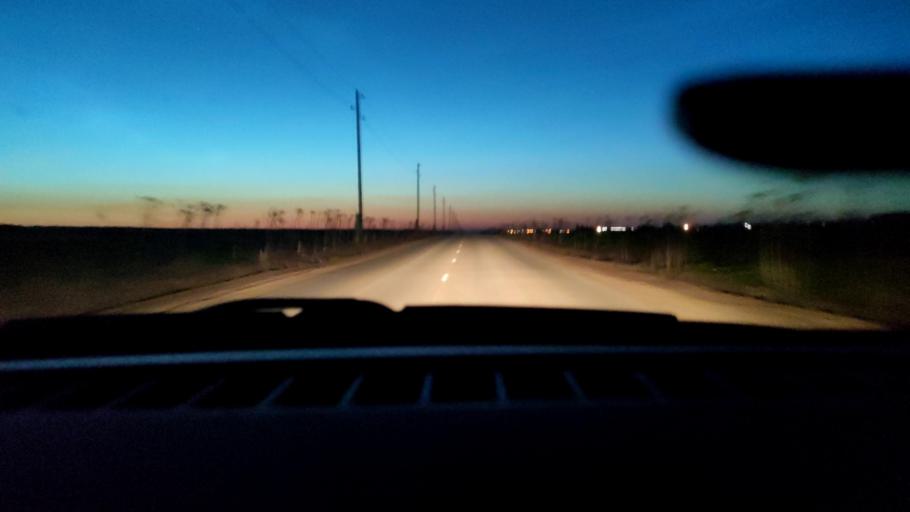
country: RU
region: Perm
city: Kultayevo
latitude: 57.8846
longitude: 55.9891
